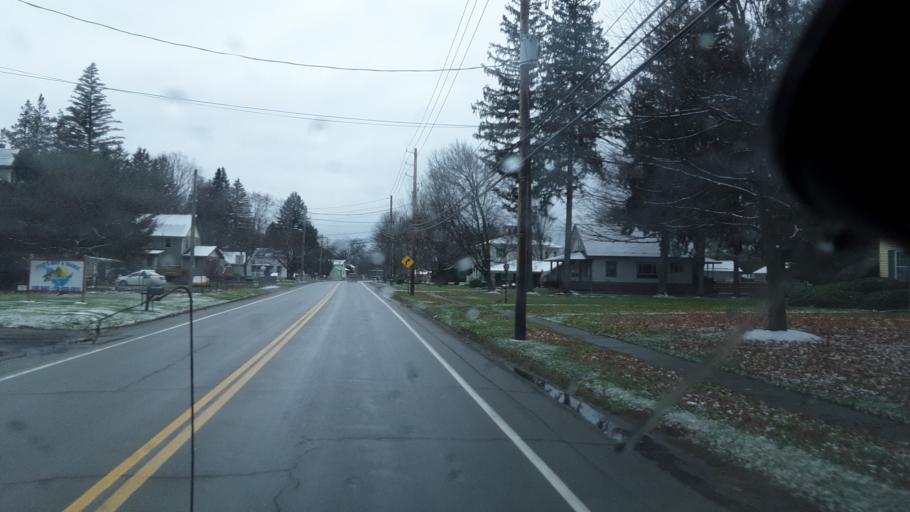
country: US
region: New York
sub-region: Cattaraugus County
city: Portville
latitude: 42.0433
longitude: -78.3461
